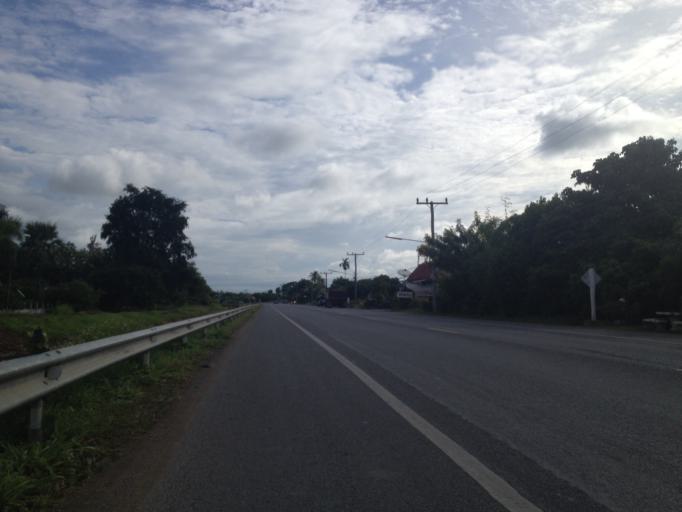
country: TH
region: Chiang Mai
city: San Pa Tong
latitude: 18.6468
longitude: 98.8513
